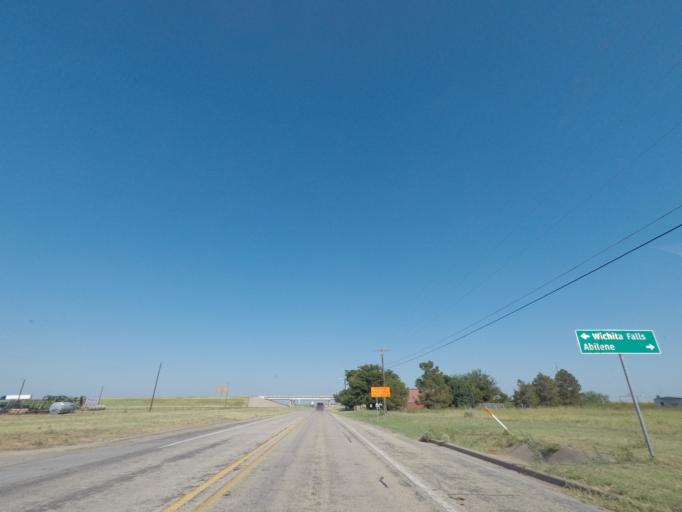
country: US
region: Texas
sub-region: Baylor County
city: Seymour
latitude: 33.5959
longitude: -99.2446
